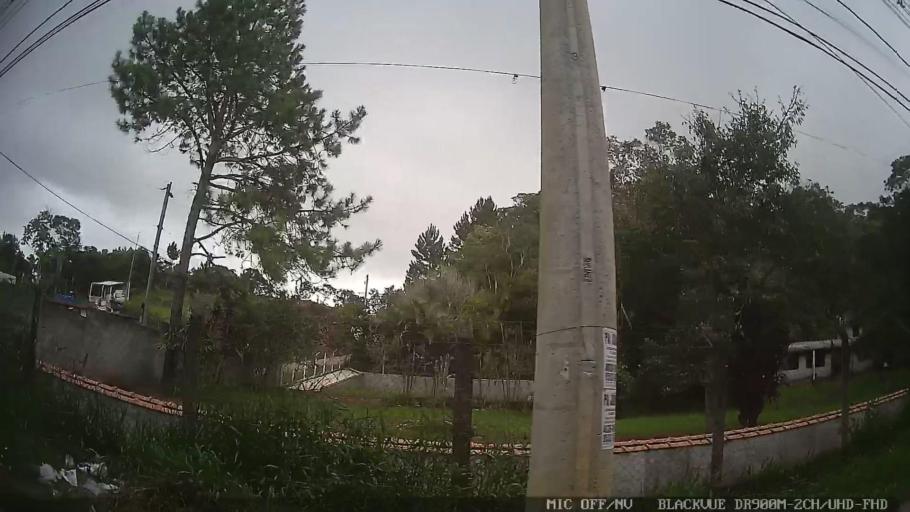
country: BR
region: Sao Paulo
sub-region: Biritiba-Mirim
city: Biritiba Mirim
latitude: -23.5465
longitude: -46.0860
